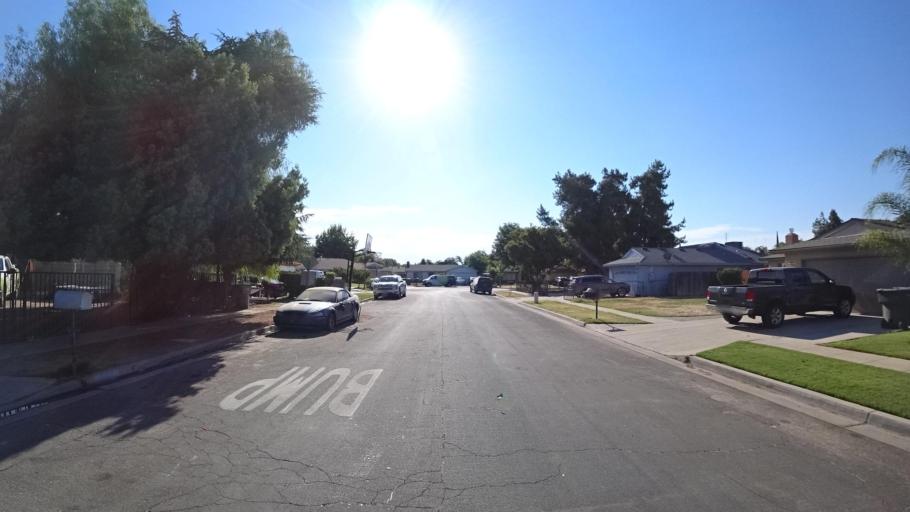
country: US
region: California
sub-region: Fresno County
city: Fresno
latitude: 36.7098
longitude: -119.7421
